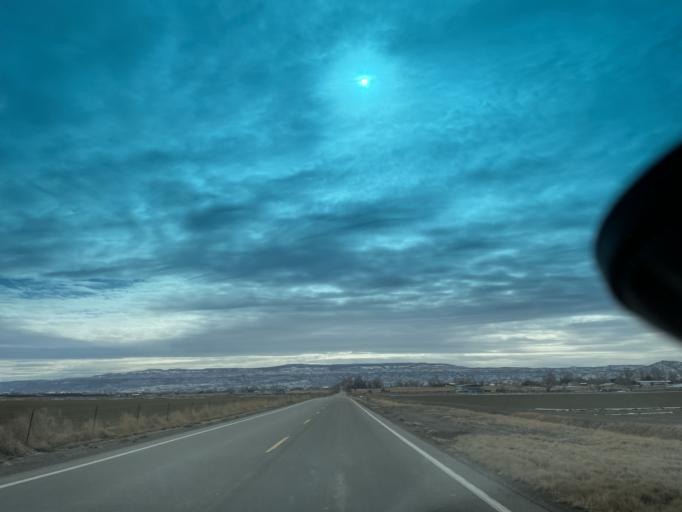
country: US
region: Colorado
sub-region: Mesa County
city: Loma
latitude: 39.2330
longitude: -108.8130
